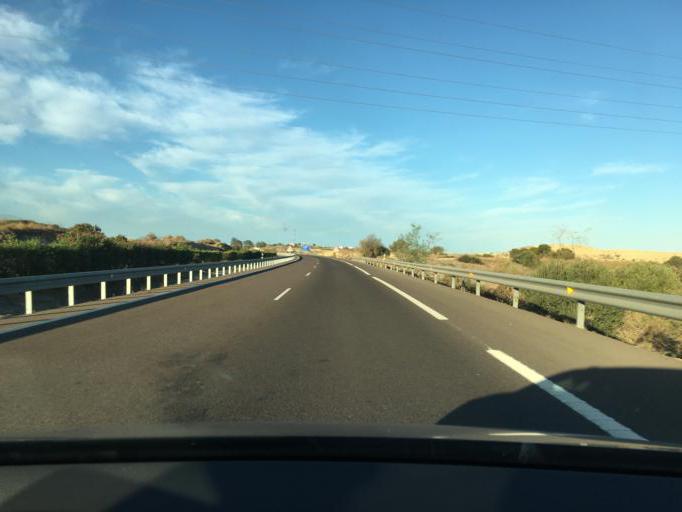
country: ES
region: Andalusia
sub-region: Provincia de Almeria
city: Turre
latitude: 37.1793
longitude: -1.9288
